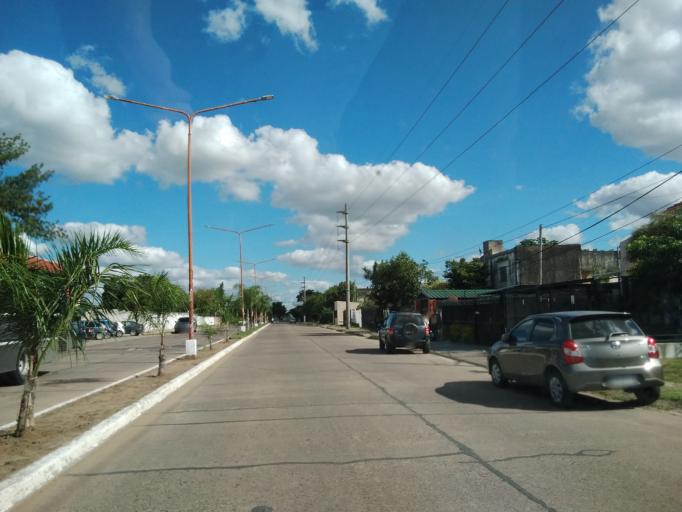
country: AR
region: Corrientes
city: Corrientes
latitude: -27.4907
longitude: -58.8260
